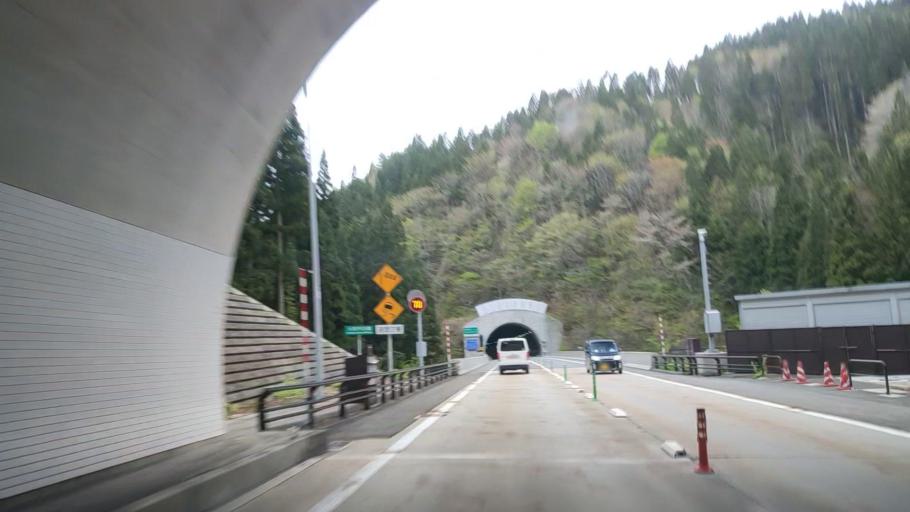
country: JP
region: Akita
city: Odate
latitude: 40.3397
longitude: 140.6224
